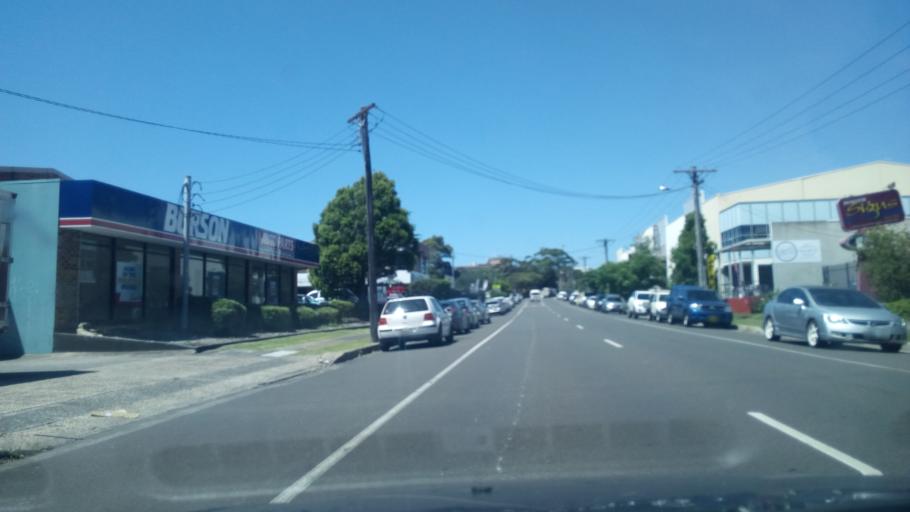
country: AU
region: New South Wales
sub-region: Wollongong
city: Wollongong
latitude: -34.4361
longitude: 150.8875
